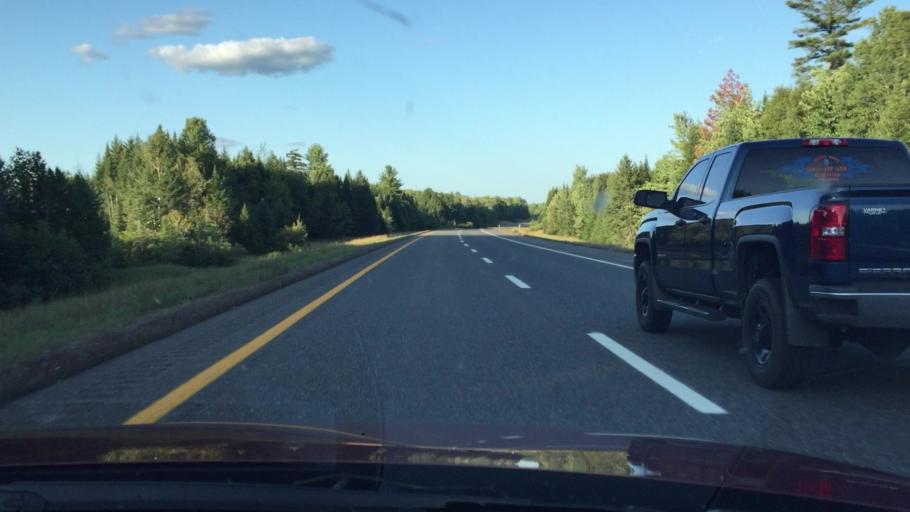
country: US
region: Maine
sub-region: Penobscot County
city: Patten
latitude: 46.0433
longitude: -68.2591
